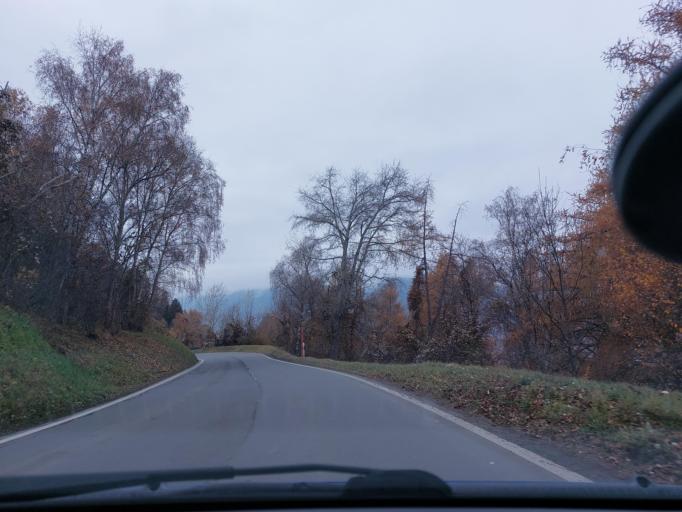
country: CH
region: Valais
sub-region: Conthey District
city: Basse-Nendaz
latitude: 46.1935
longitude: 7.2951
